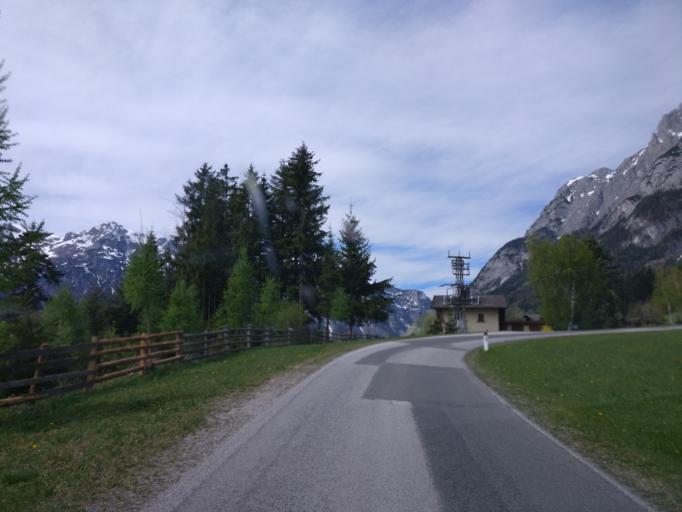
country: AT
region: Salzburg
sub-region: Politischer Bezirk Sankt Johann im Pongau
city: Pfarrwerfen
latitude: 47.4758
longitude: 13.2056
